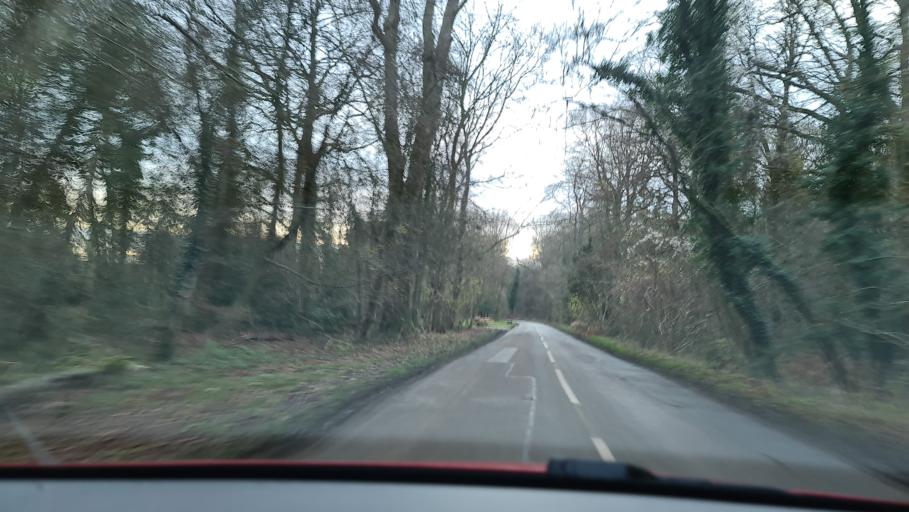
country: GB
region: England
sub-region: Buckinghamshire
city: Princes Risborough
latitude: 51.7081
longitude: -0.7860
